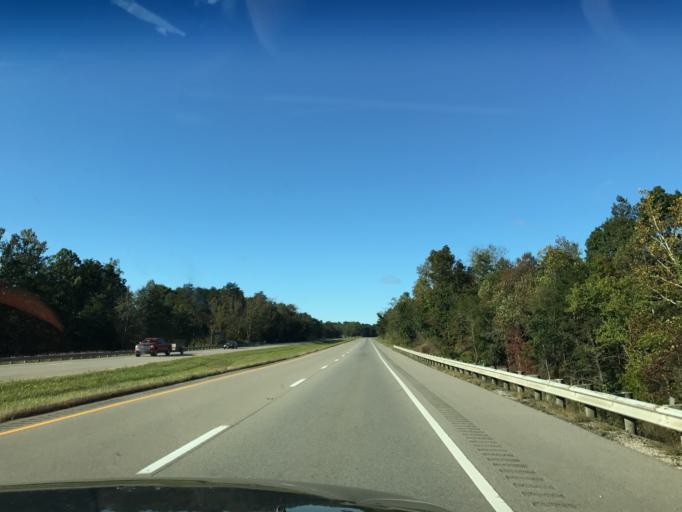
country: US
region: West Virginia
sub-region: Wood County
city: Washington
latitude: 39.2476
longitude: -81.7169
